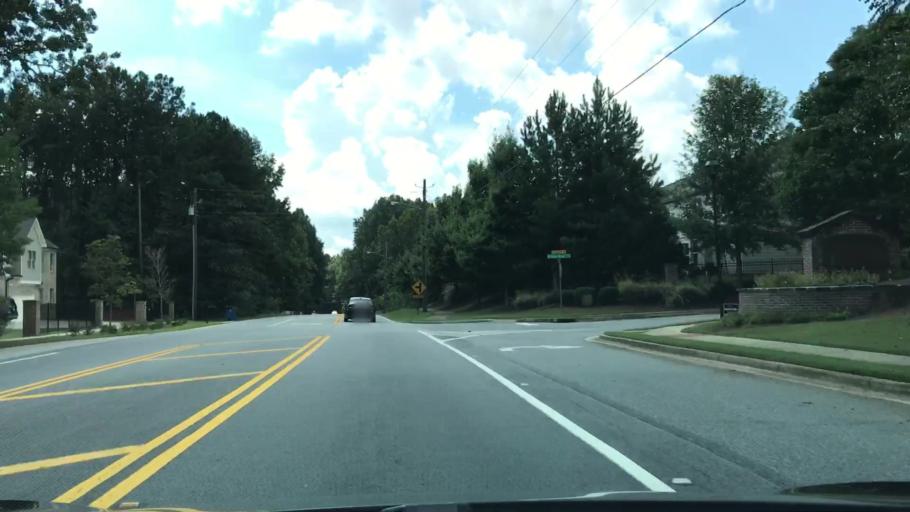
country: US
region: Georgia
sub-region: Gwinnett County
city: Snellville
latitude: 33.9043
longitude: -84.0684
